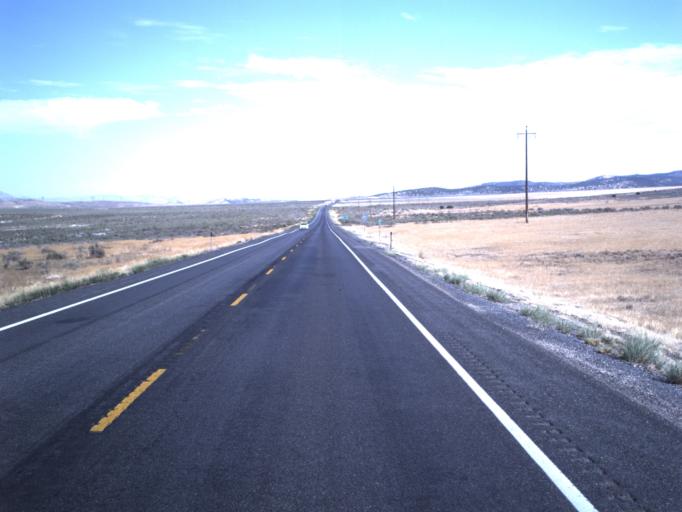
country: US
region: Utah
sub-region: Sanpete County
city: Gunnison
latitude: 39.2874
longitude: -111.8842
